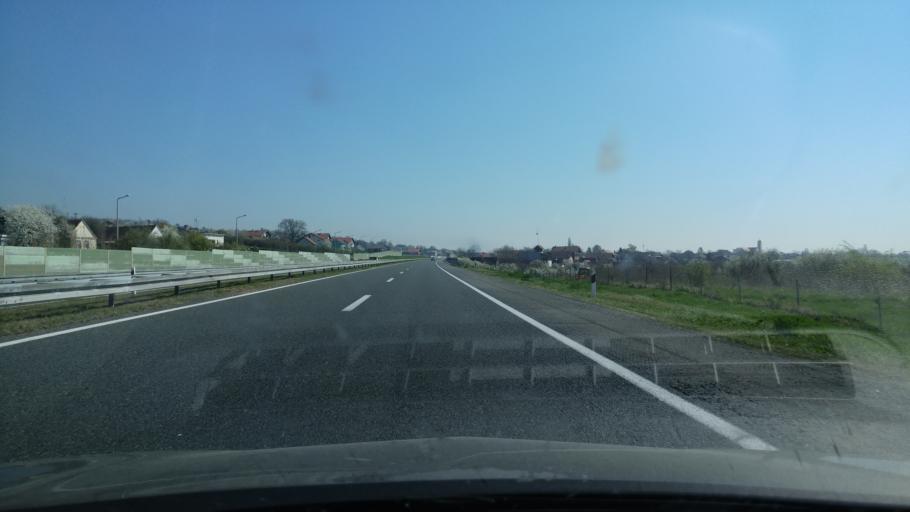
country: HR
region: Brodsko-Posavska
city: Slobodnica
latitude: 45.1778
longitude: 17.9671
